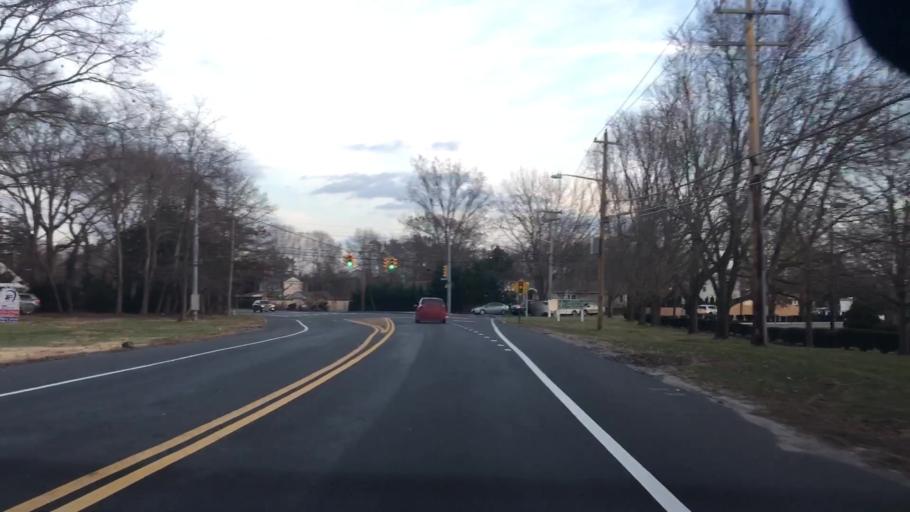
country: US
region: New York
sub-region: Suffolk County
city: Central Islip
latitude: 40.8051
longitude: -73.1982
